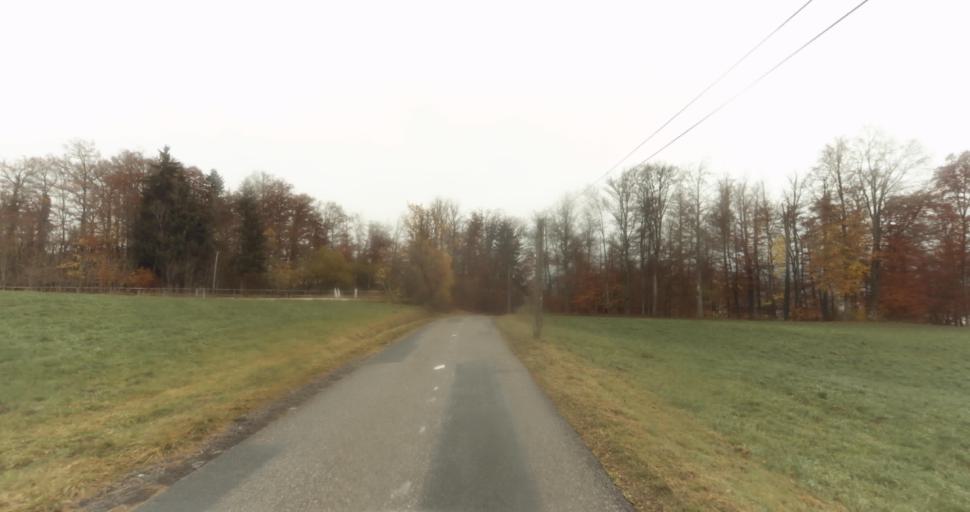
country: FR
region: Rhone-Alpes
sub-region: Departement de la Haute-Savoie
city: Evires
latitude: 46.0577
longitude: 6.2251
